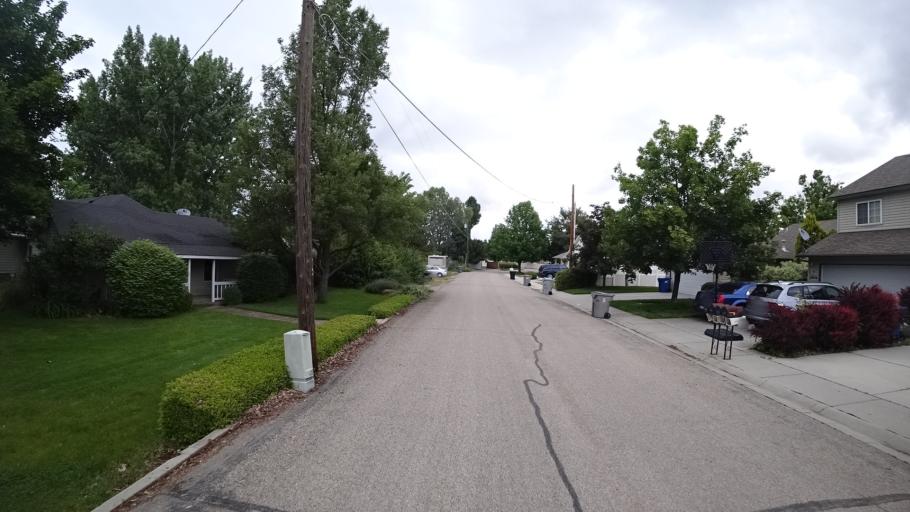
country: US
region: Idaho
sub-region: Ada County
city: Eagle
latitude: 43.6736
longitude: -116.2943
